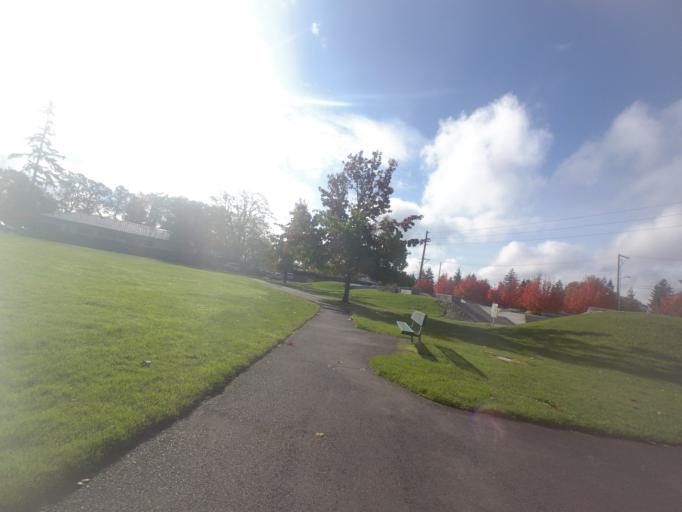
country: US
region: Washington
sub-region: Pierce County
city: Lakewood
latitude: 47.1755
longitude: -122.5173
